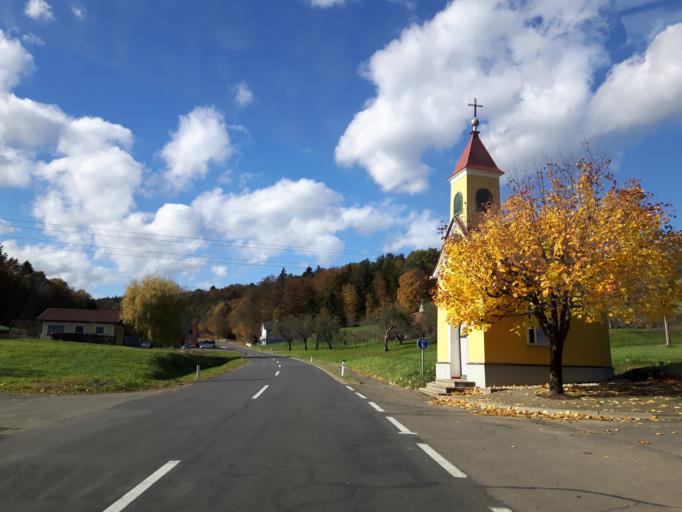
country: AT
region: Styria
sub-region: Politischer Bezirk Suedoststeiermark
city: Baumgarten bei Gnas
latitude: 46.9387
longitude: 15.7656
